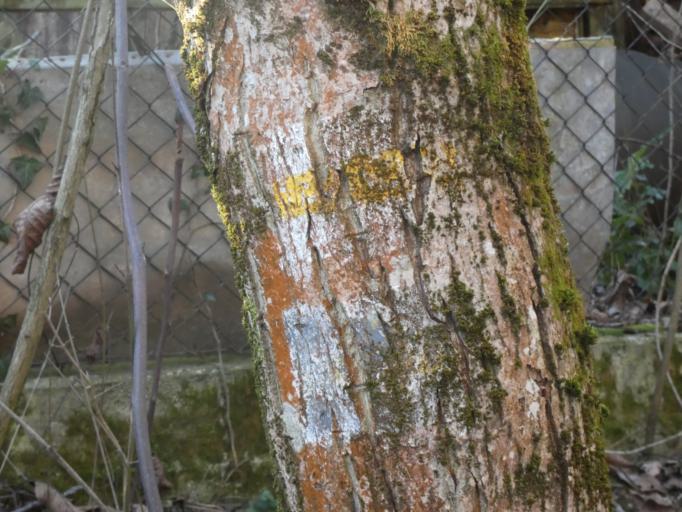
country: HU
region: Pest
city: Nagymaros
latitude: 47.7819
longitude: 18.9450
